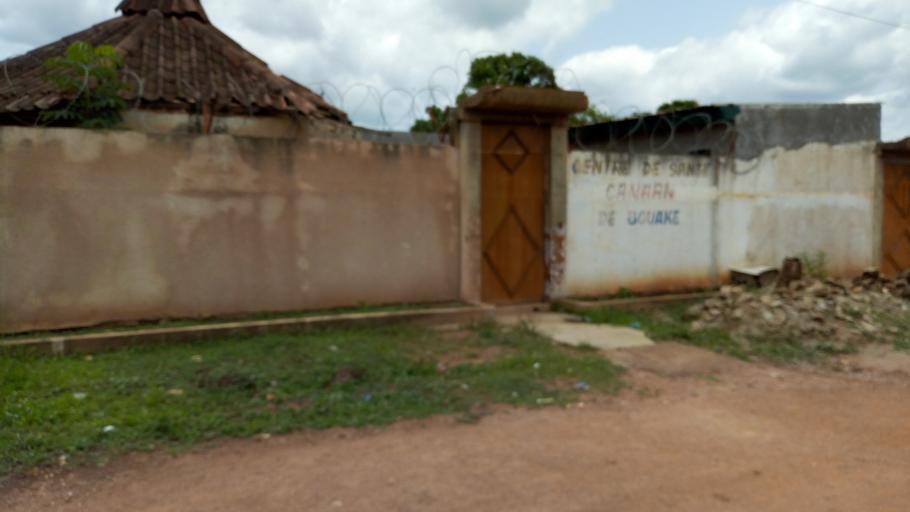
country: CI
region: Vallee du Bandama
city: Bouake
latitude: 7.6479
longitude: -5.0268
